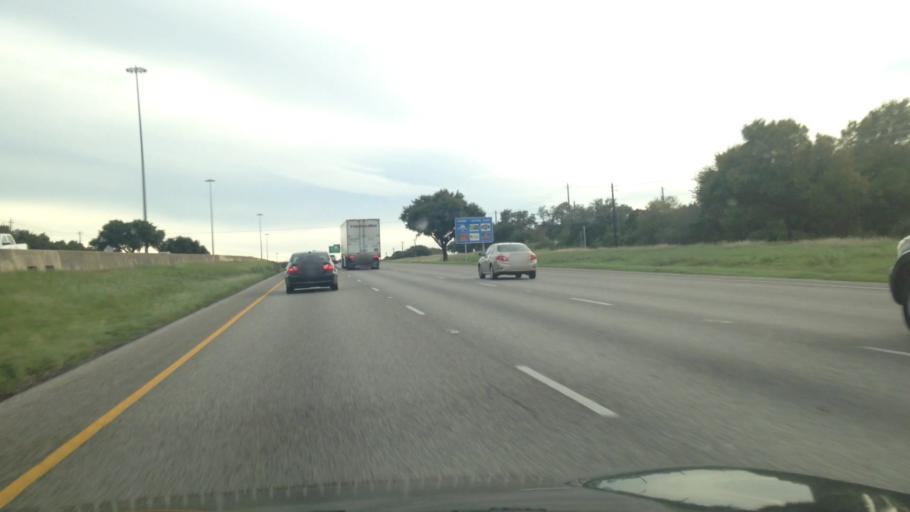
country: US
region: Texas
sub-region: Travis County
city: Onion Creek
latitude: 30.1288
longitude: -97.8006
